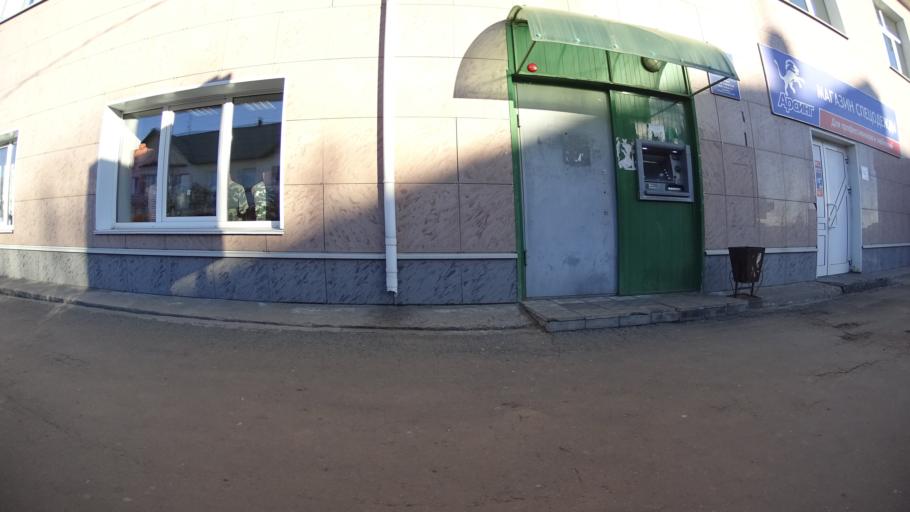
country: RU
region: Chelyabinsk
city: Troitsk
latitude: 54.0889
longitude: 61.5584
